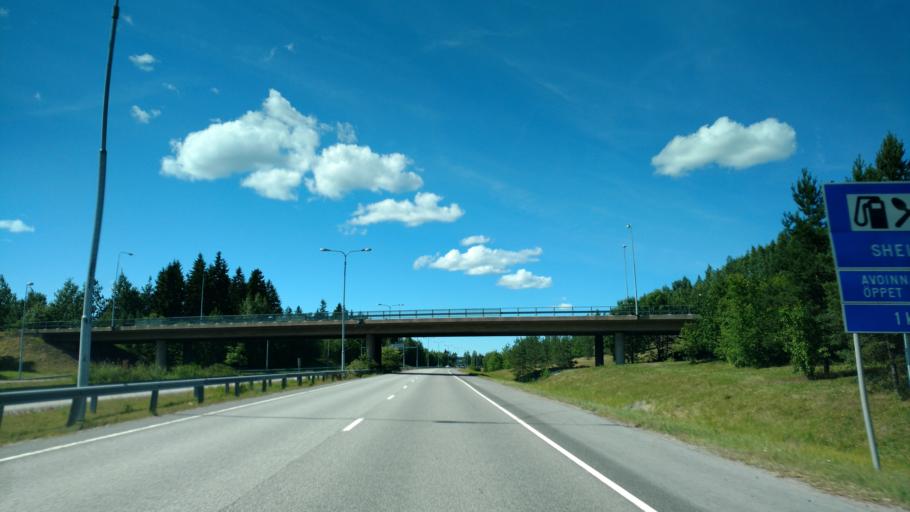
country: FI
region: Varsinais-Suomi
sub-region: Turku
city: Turku
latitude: 60.4794
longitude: 22.3358
